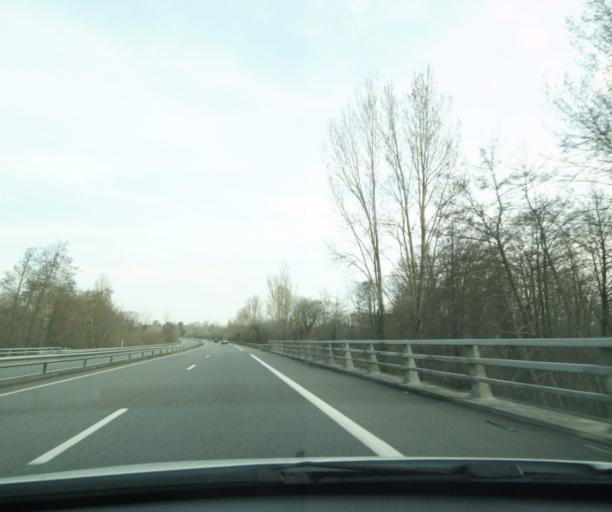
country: FR
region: Midi-Pyrenees
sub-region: Departement des Hautes-Pyrenees
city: Juillan
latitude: 43.2117
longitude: 0.0359
